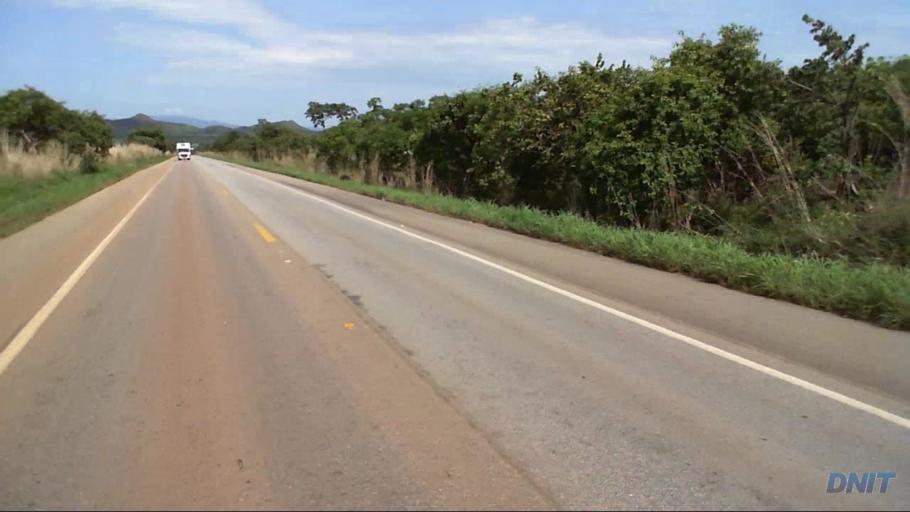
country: BR
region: Goias
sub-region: Barro Alto
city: Barro Alto
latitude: -15.1965
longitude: -48.7651
